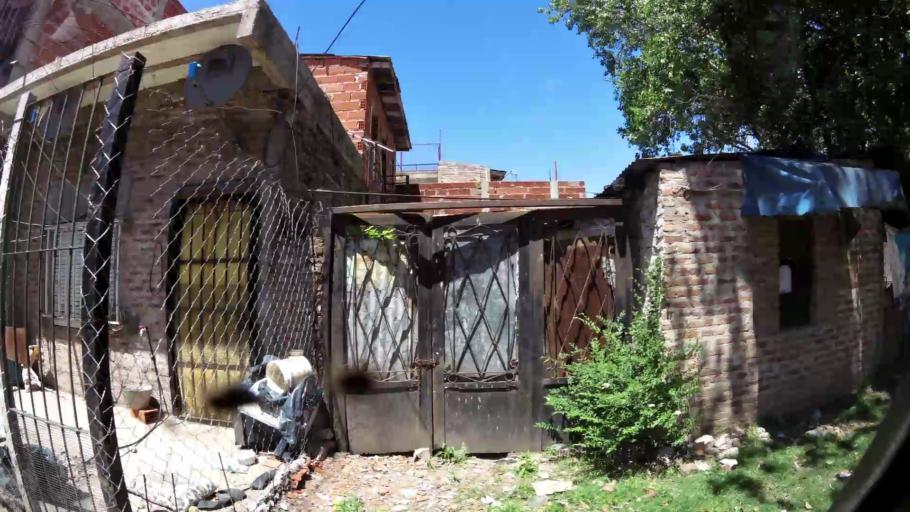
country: AR
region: Buenos Aires
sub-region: Partido de Lanus
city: Lanus
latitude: -34.7257
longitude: -58.3307
